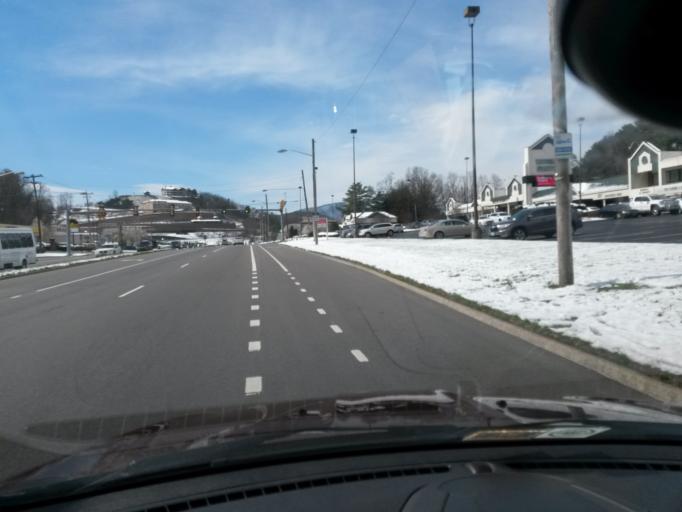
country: US
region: Virginia
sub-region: Roanoke County
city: Narrows
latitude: 37.2353
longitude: -79.9704
